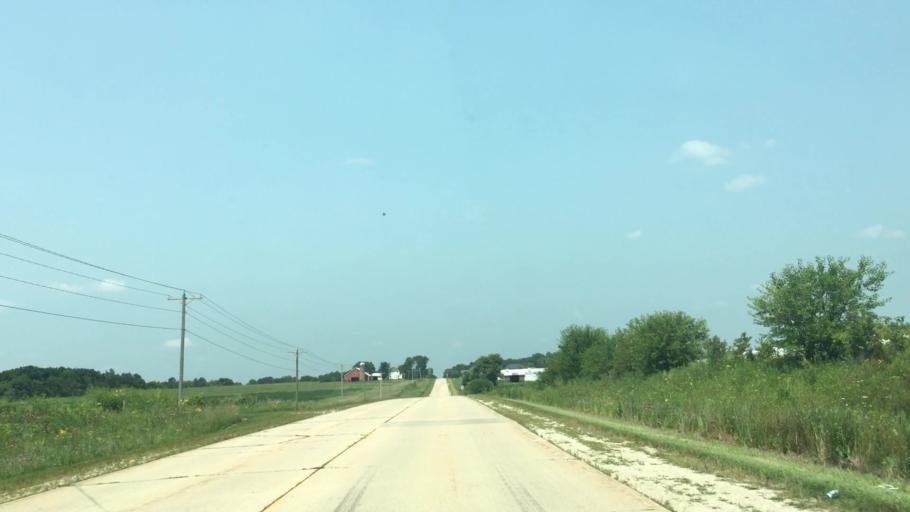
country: US
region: Iowa
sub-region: Fayette County
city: Oelwein
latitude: 42.6678
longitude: -91.8938
